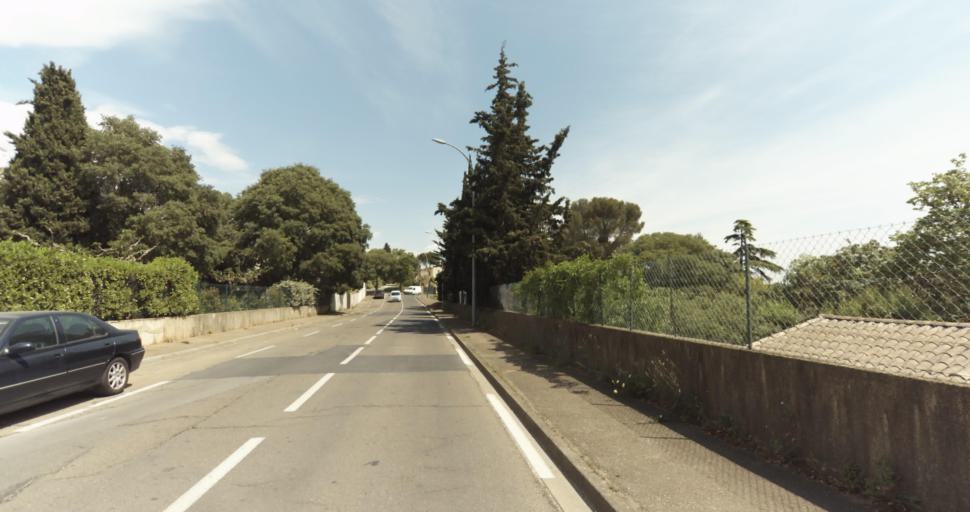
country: FR
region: Languedoc-Roussillon
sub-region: Departement du Gard
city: Nimes
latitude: 43.8472
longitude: 4.3833
